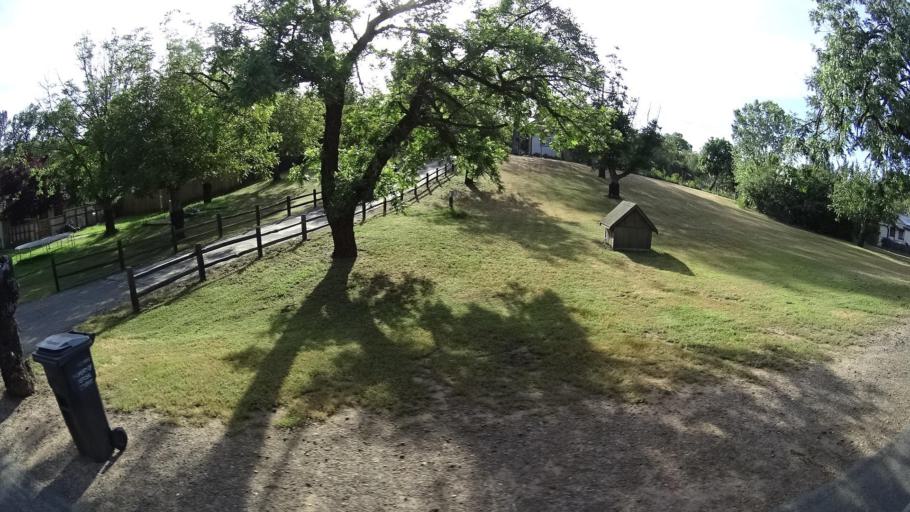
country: US
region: California
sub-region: Lake County
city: North Lakeport
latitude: 39.0782
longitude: -122.9170
